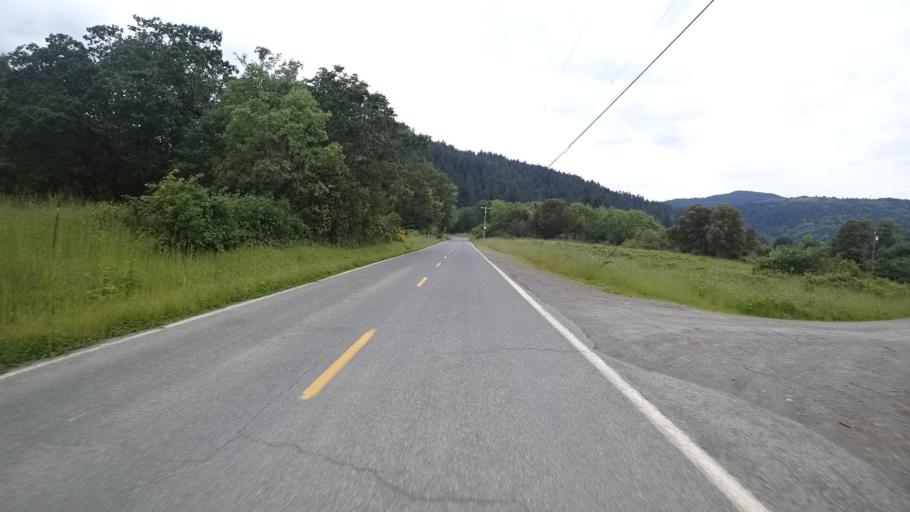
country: US
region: California
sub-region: Humboldt County
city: Willow Creek
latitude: 41.0862
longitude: -123.7074
